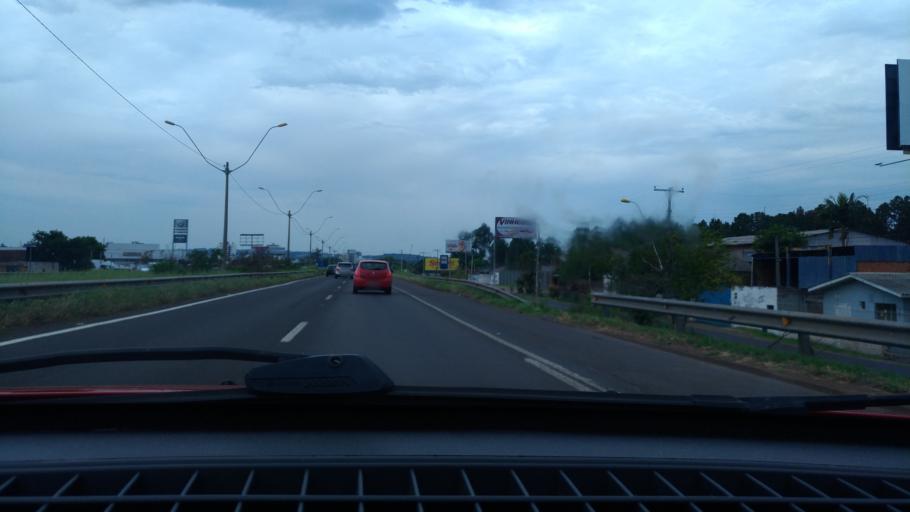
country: BR
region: Rio Grande do Sul
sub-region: Sao Leopoldo
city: Sao Leopoldo
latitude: -29.7523
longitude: -51.1516
